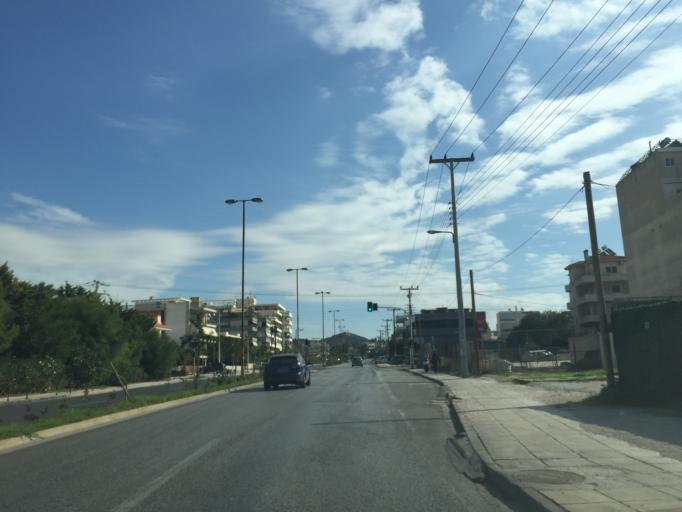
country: GR
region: Attica
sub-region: Nomarchia Anatolikis Attikis
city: Voula
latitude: 37.8337
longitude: 23.7751
